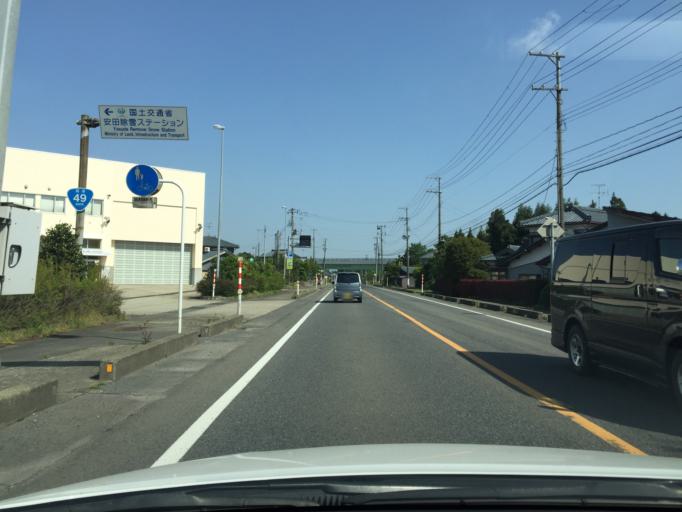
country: JP
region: Niigata
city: Gosen
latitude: 37.7503
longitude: 139.2515
